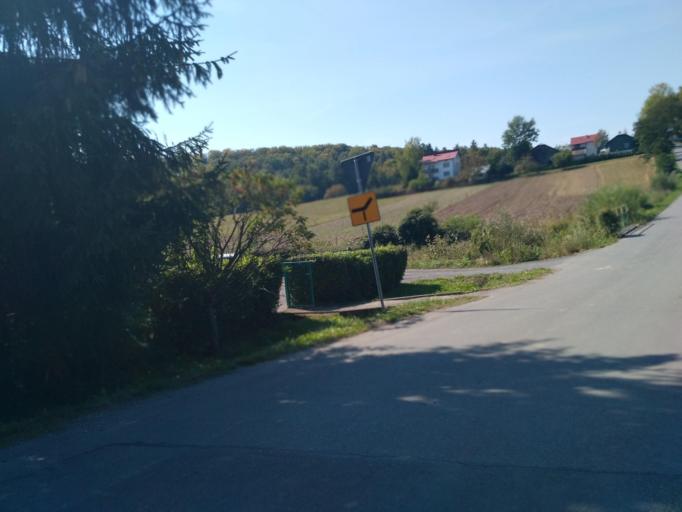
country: PL
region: Subcarpathian Voivodeship
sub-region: Powiat brzozowski
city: Niebocko
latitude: 49.6542
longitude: 22.1387
